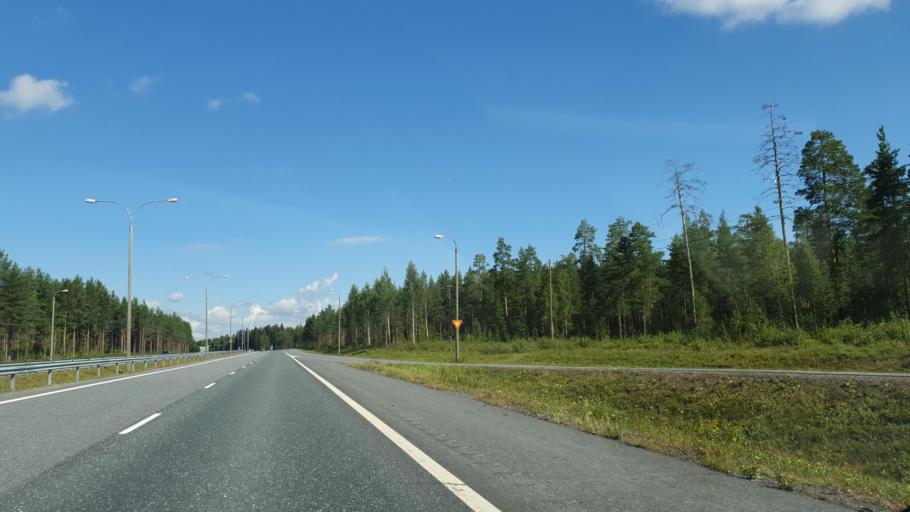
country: FI
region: Northern Savo
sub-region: Ylae-Savo
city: Iisalmi
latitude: 63.5494
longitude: 27.2531
